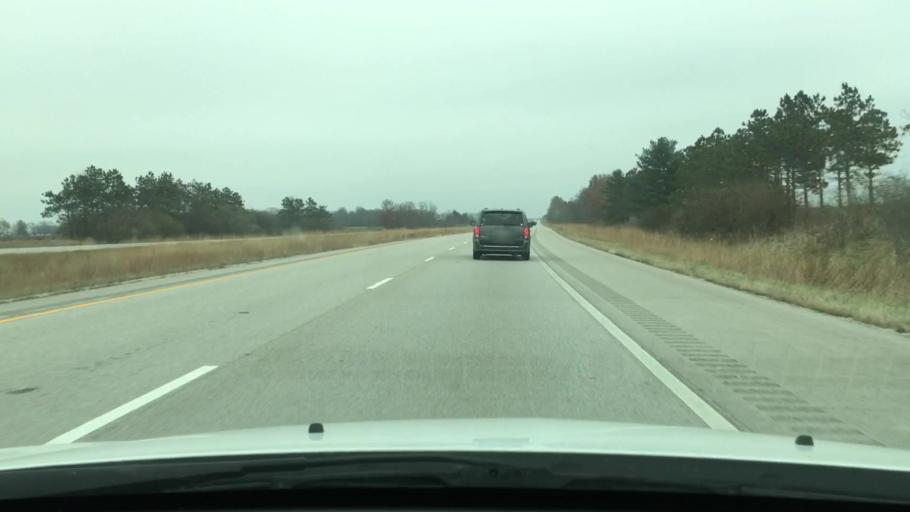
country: US
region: Illinois
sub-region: Sangamon County
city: New Berlin
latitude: 39.7397
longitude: -89.9693
